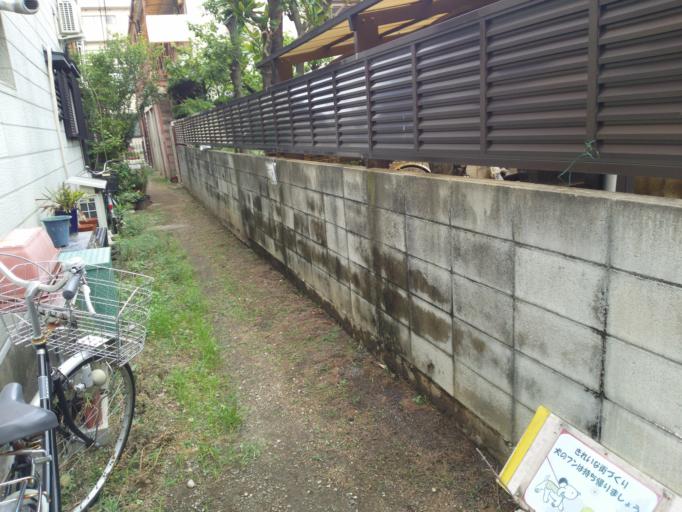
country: JP
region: Osaka
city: Toyonaka
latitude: 34.7563
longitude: 135.4483
